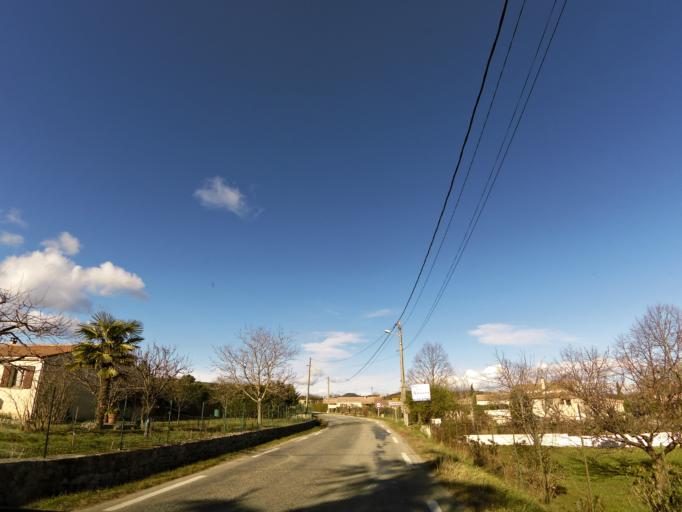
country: FR
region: Languedoc-Roussillon
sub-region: Departement du Gard
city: Sauve
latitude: 43.9865
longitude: 3.9518
